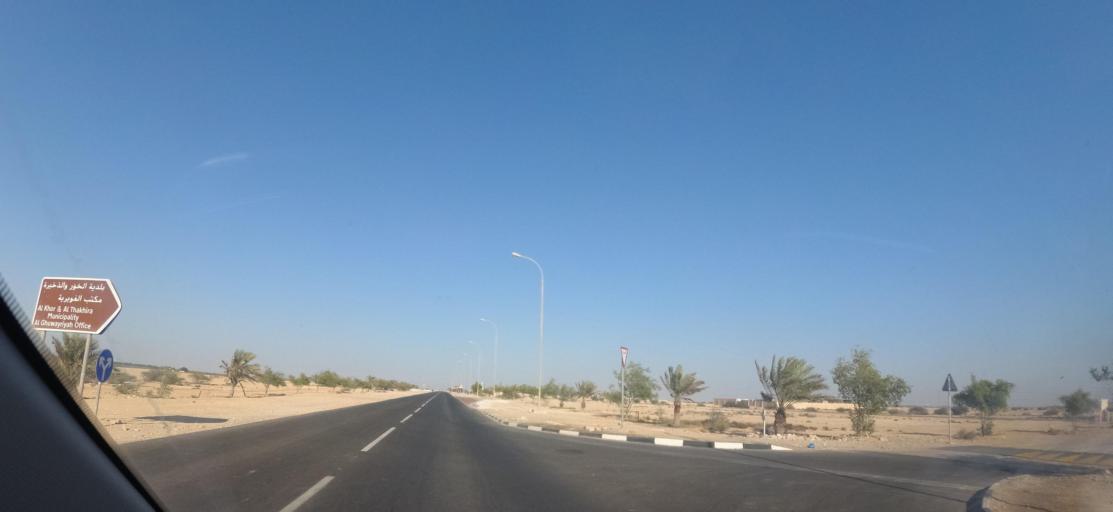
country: QA
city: Al Ghuwayriyah
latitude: 25.8328
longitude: 51.2527
